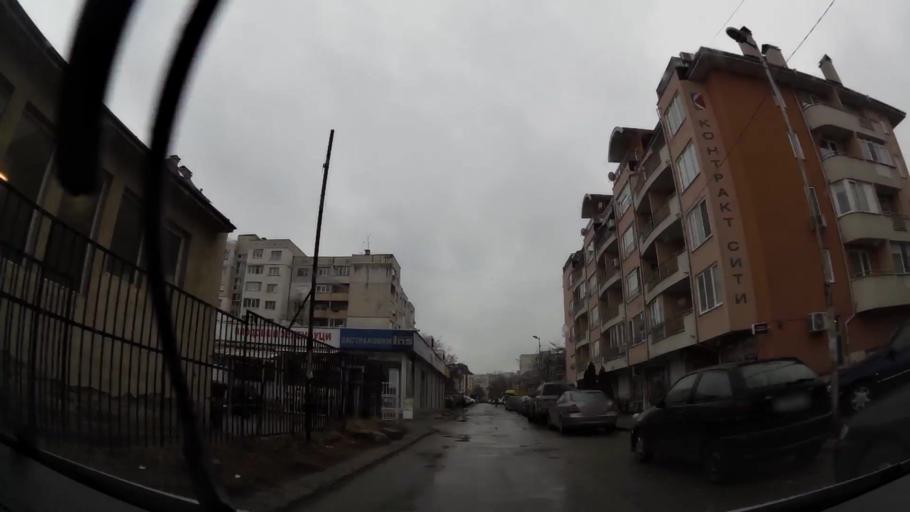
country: BG
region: Sofia-Capital
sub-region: Stolichna Obshtina
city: Sofia
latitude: 42.6370
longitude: 23.3776
